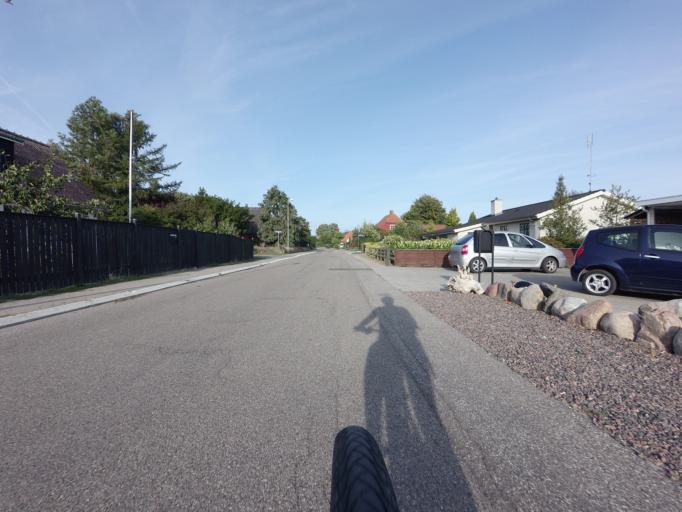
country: DK
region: Zealand
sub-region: Stevns Kommune
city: Store Heddinge
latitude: 55.2543
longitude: 12.3631
